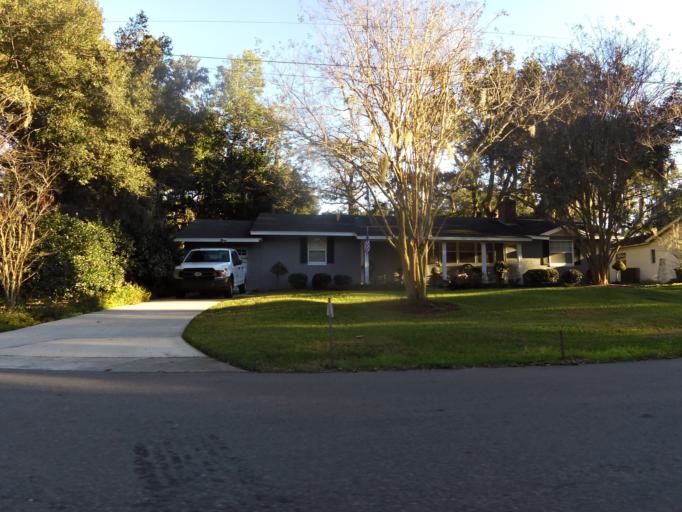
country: US
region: Florida
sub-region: Duval County
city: Jacksonville
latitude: 30.2690
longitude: -81.7047
